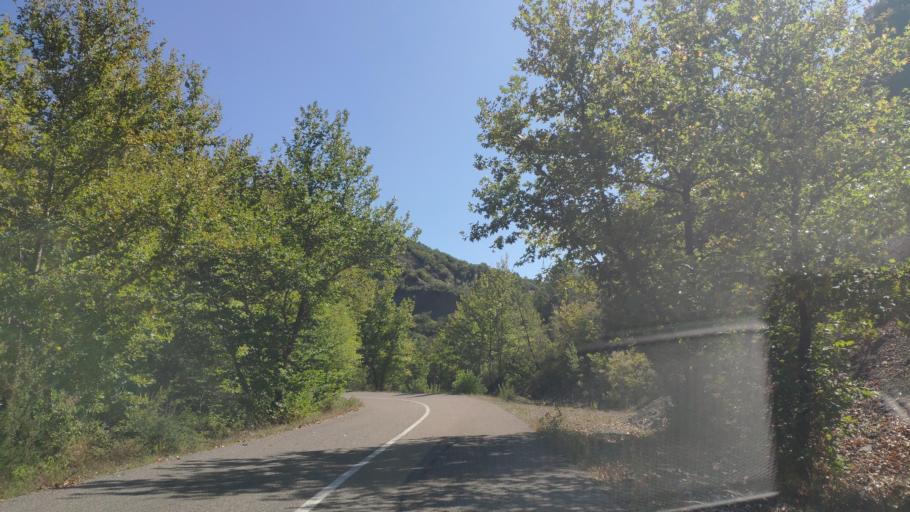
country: GR
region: Central Greece
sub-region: Nomos Evrytanias
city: Kerasochori
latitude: 39.0003
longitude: 21.5167
